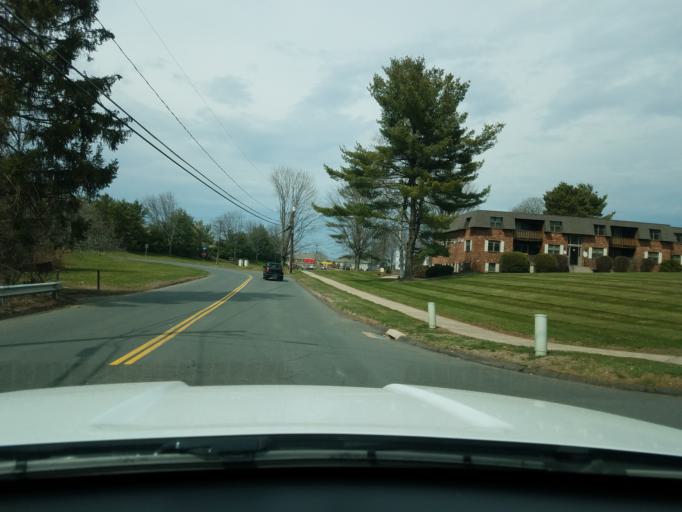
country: US
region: Connecticut
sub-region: Hartford County
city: Newington
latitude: 41.6619
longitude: -72.7170
